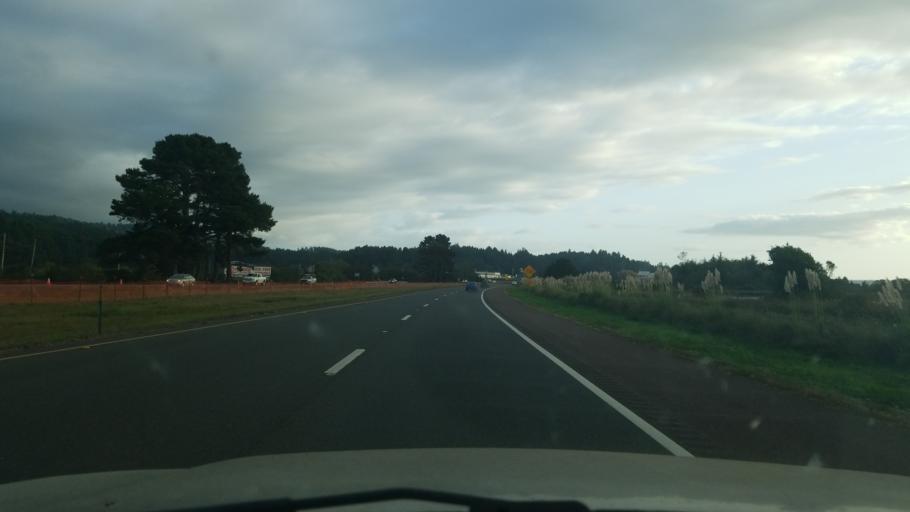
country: US
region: California
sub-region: Humboldt County
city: Bayside
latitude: 40.8337
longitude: -124.0823
